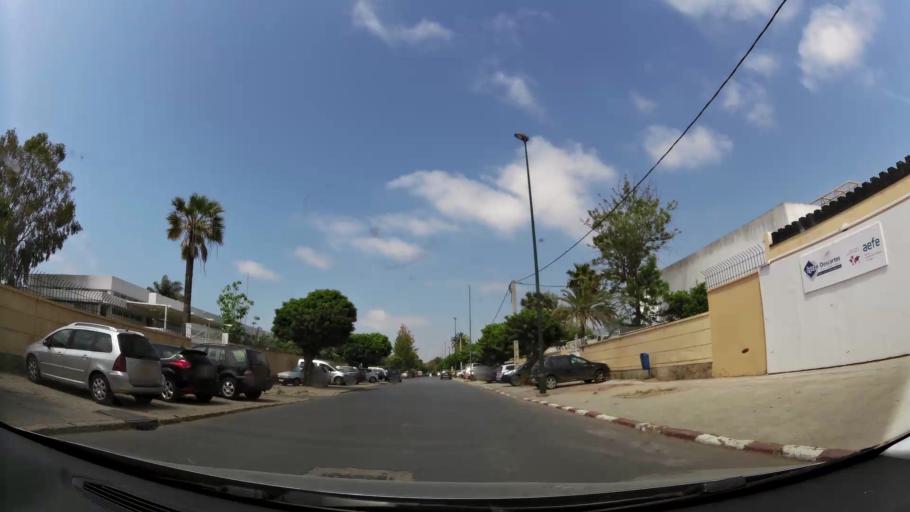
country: MA
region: Rabat-Sale-Zemmour-Zaer
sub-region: Rabat
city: Rabat
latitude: 33.9901
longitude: -6.8456
